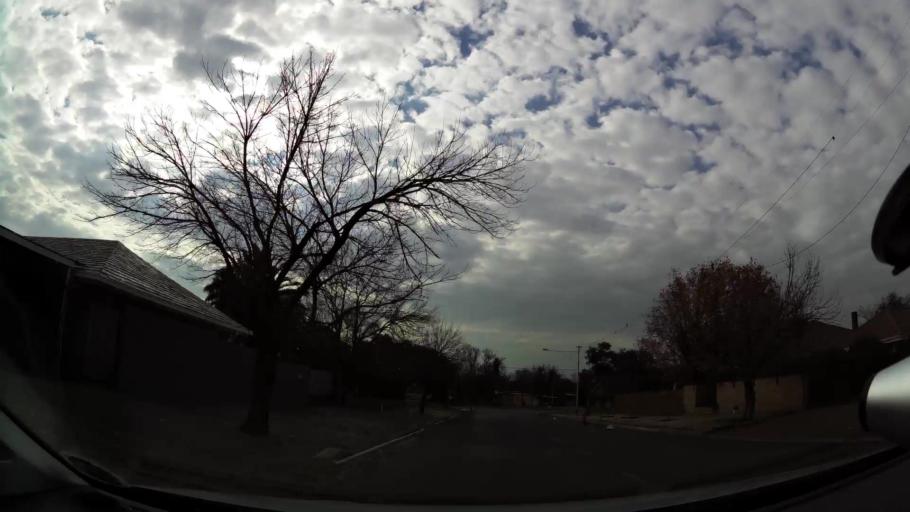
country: ZA
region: Orange Free State
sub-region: Mangaung Metropolitan Municipality
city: Bloemfontein
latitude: -29.0900
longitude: 26.2340
